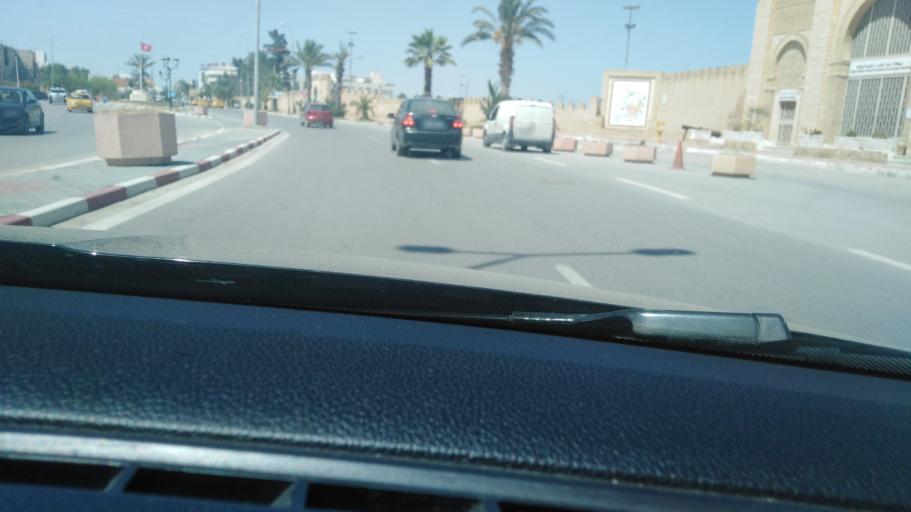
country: TN
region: Al Qayrawan
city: Kairouan
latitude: 35.6864
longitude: 10.0974
